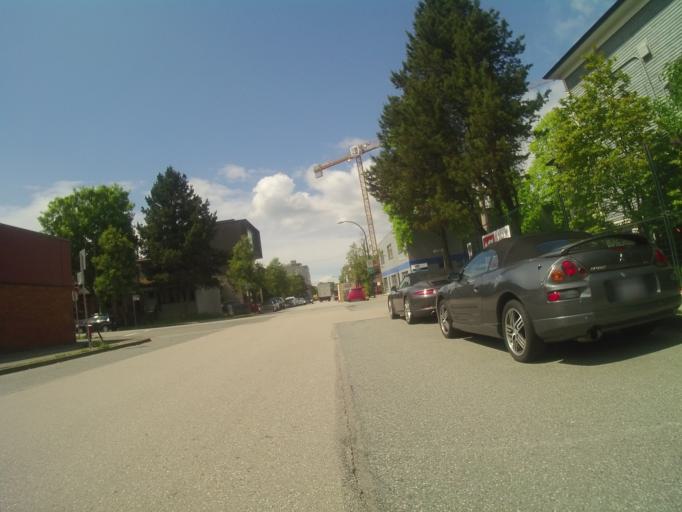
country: CA
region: British Columbia
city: Vancouver
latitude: 49.2666
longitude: -123.1089
